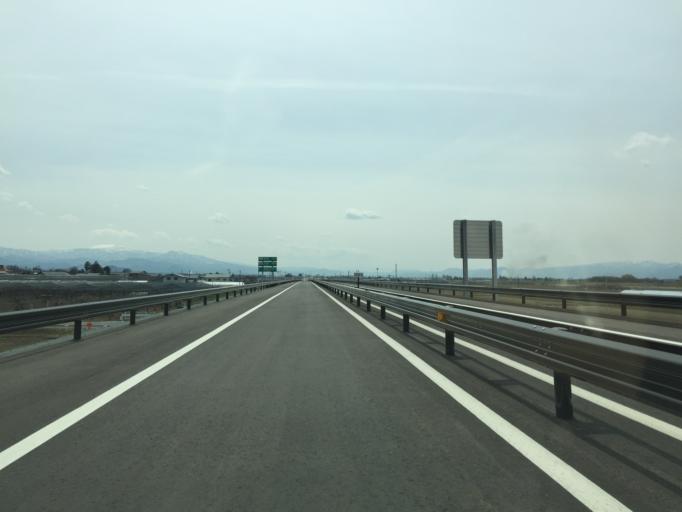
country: JP
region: Yamagata
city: Higashine
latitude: 38.4352
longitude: 140.3535
